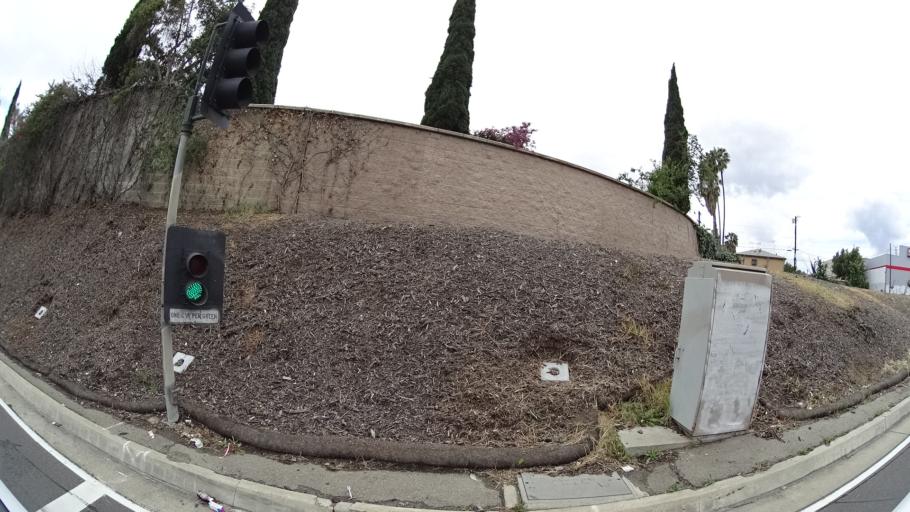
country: US
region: California
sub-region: Los Angeles County
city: Hollywood
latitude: 34.0900
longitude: -118.3065
